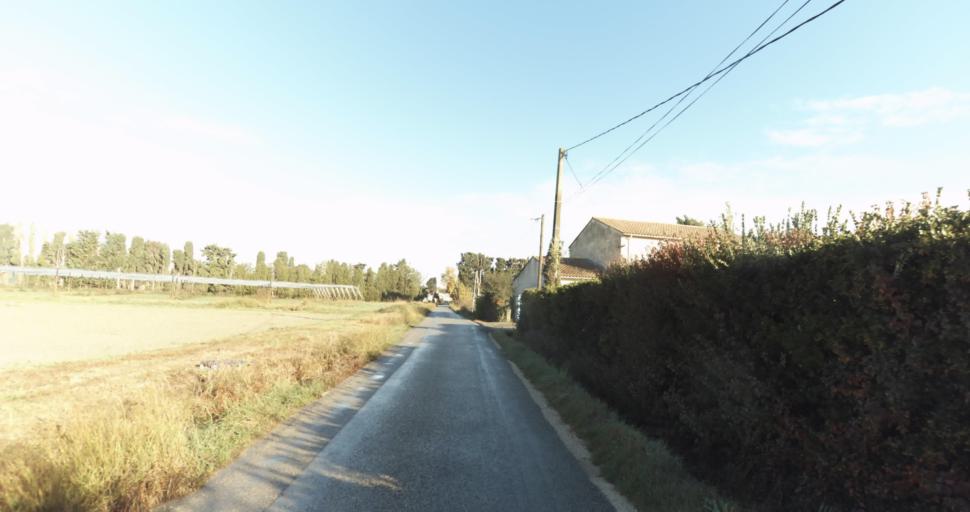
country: FR
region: Provence-Alpes-Cote d'Azur
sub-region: Departement des Bouches-du-Rhone
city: Rognonas
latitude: 43.8860
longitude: 4.7925
